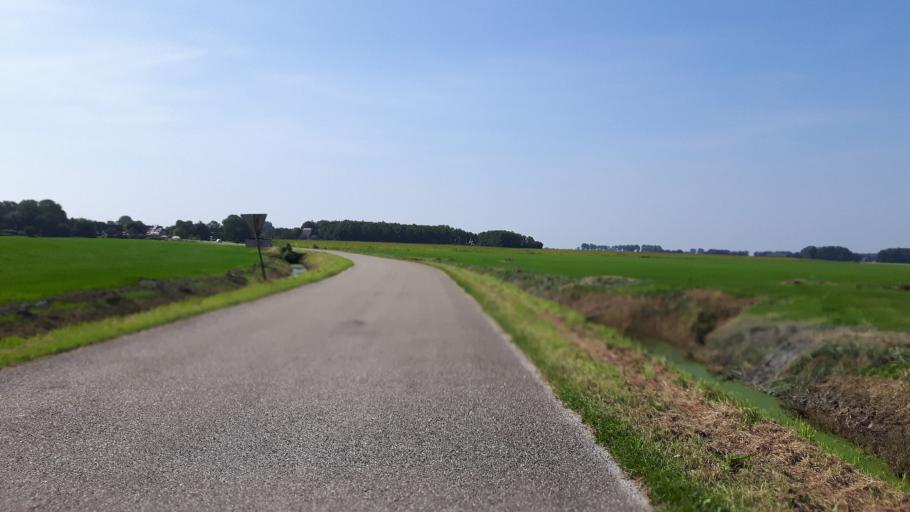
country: NL
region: Friesland
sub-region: Gemeente Ferwerderadiel
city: Hallum
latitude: 53.2962
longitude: 5.7721
